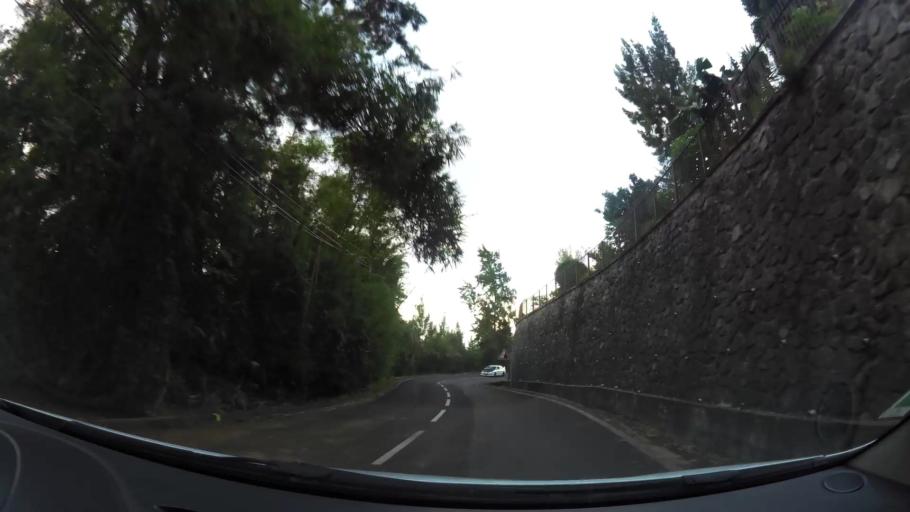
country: RE
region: Reunion
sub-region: Reunion
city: Saint-Denis
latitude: -20.9220
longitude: 55.4500
